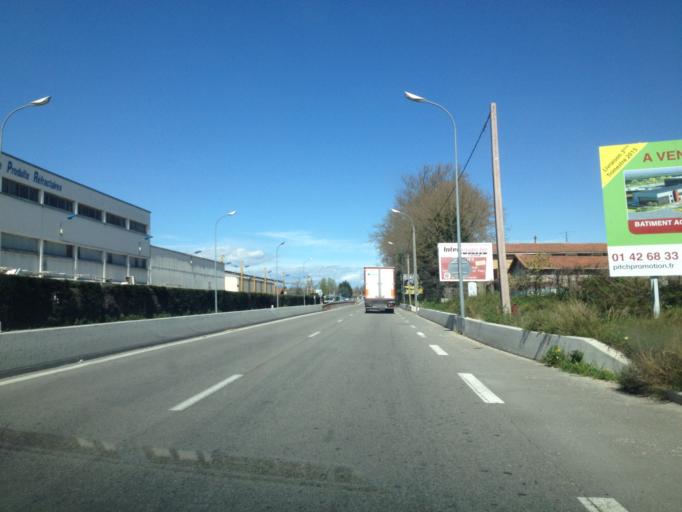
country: FR
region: Provence-Alpes-Cote d'Azur
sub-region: Departement du Vaucluse
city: Sorgues
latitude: 43.9875
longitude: 4.8620
